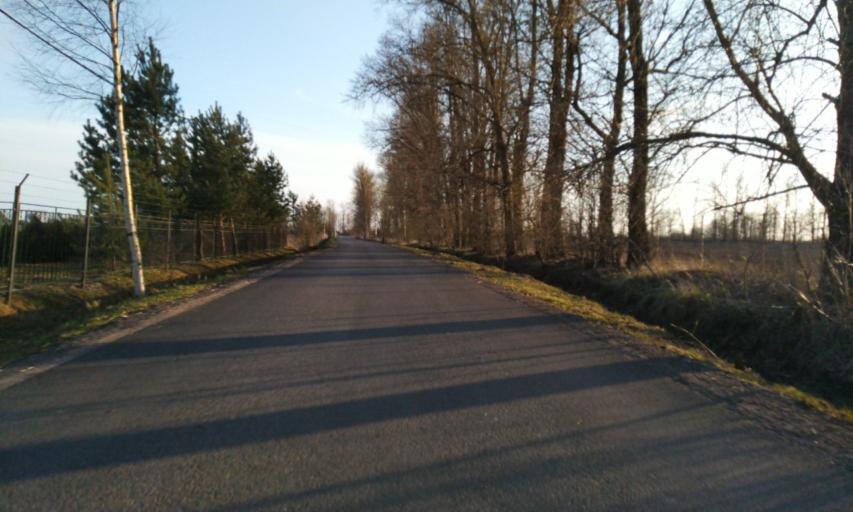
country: RU
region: Leningrad
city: Novoye Devyatkino
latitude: 60.1046
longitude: 30.4506
